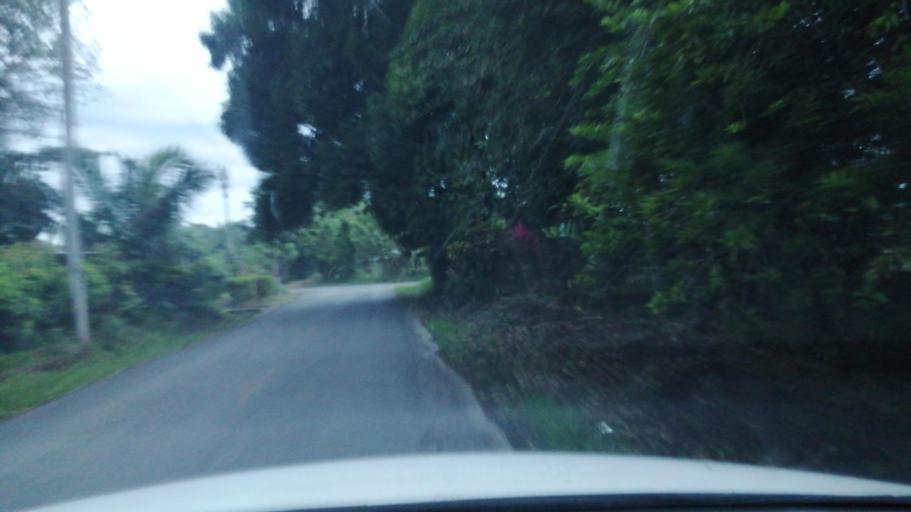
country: PA
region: Chiriqui
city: Alanje
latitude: 8.4124
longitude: -82.5038
